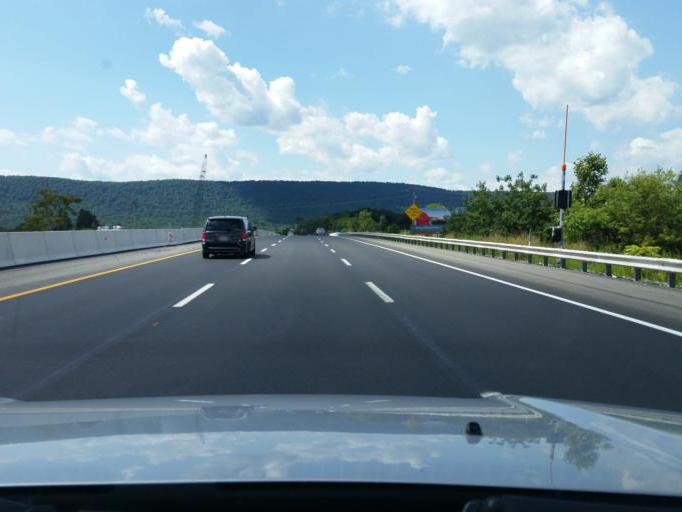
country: US
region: Pennsylvania
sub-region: Fulton County
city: McConnellsburg
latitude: 40.0512
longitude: -78.0700
